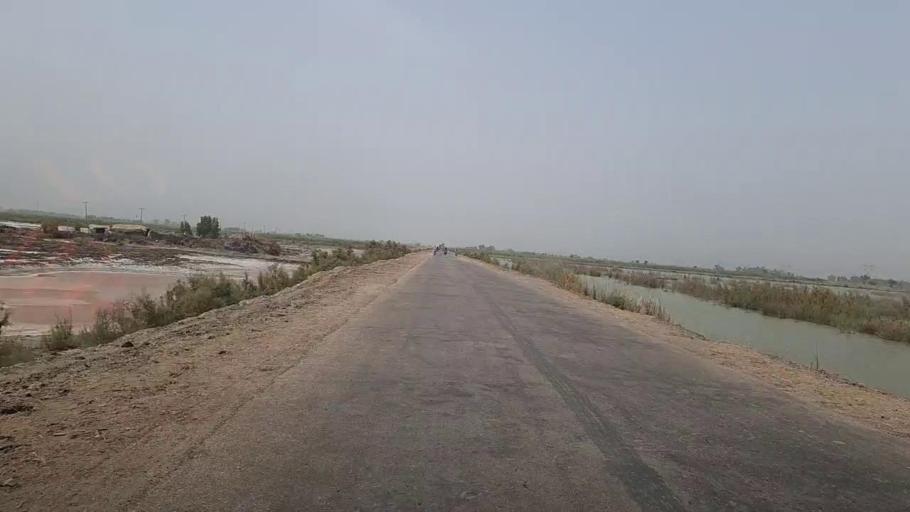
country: PK
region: Sindh
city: Radhan
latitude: 27.1579
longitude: 67.9414
